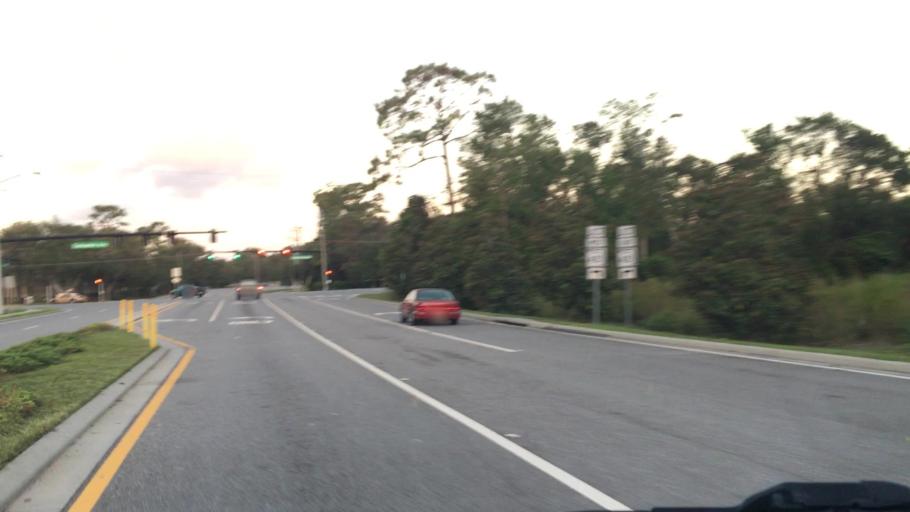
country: US
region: Florida
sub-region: Volusia County
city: Port Orange
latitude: 29.1121
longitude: -81.0242
